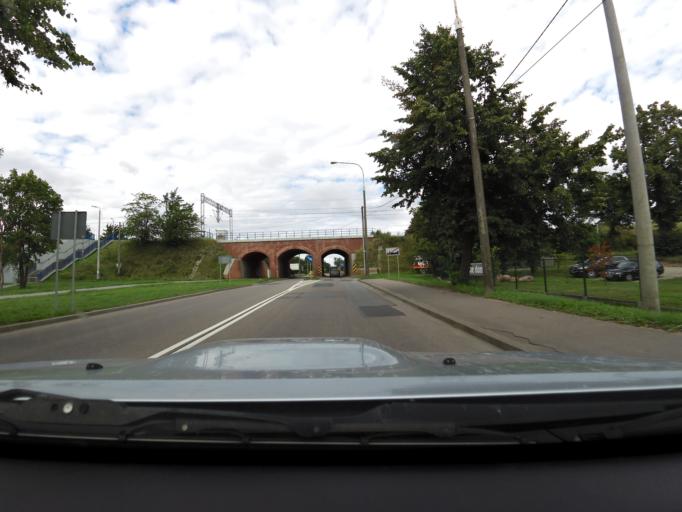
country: PL
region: Pomeranian Voivodeship
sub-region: Powiat malborski
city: Malbork
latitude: 54.0461
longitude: 19.0247
